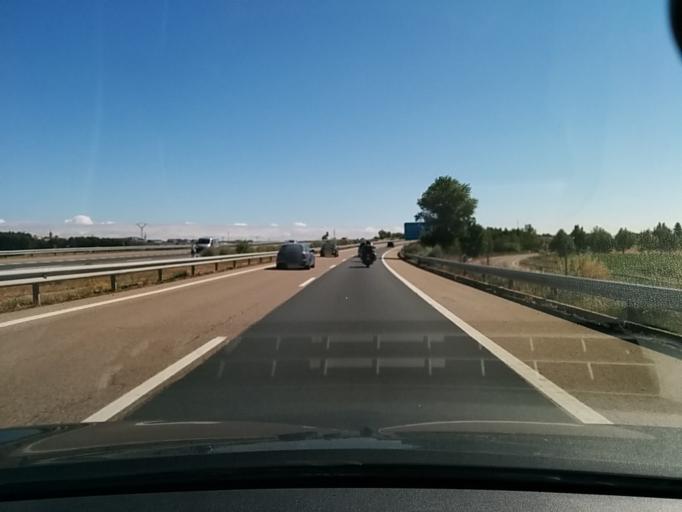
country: ES
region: Aragon
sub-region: Provincia de Huesca
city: Almudebar
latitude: 42.0305
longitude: -0.5908
